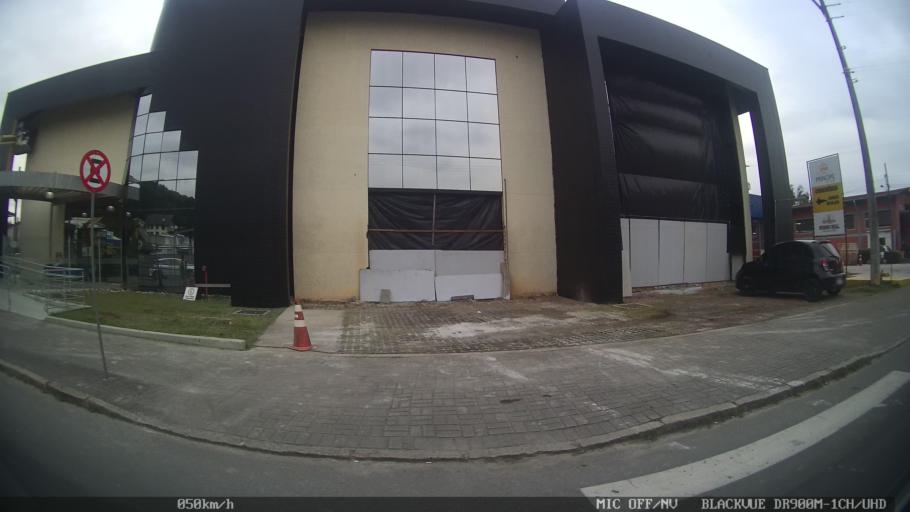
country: BR
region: Santa Catarina
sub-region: Joinville
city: Joinville
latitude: -26.2856
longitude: -48.8699
